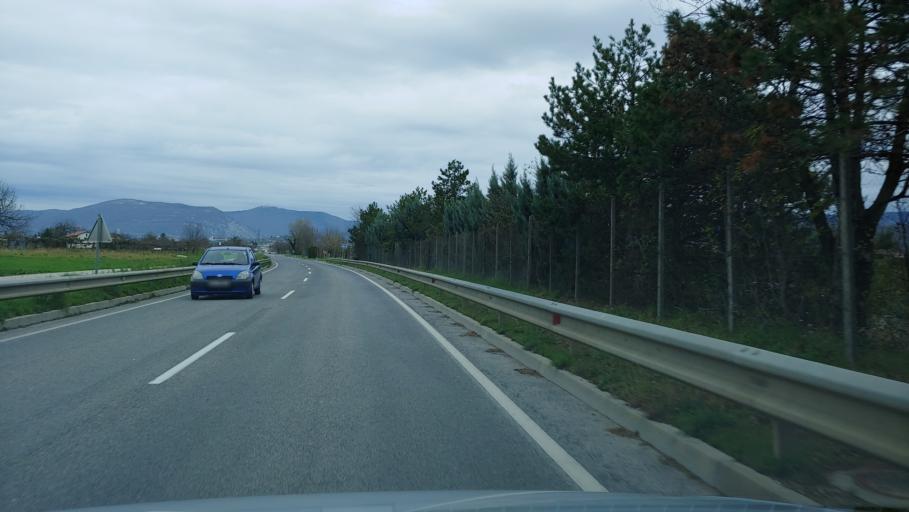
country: SI
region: Sempeter-Vrtojba
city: Vrtojba
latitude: 45.9107
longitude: 13.6273
